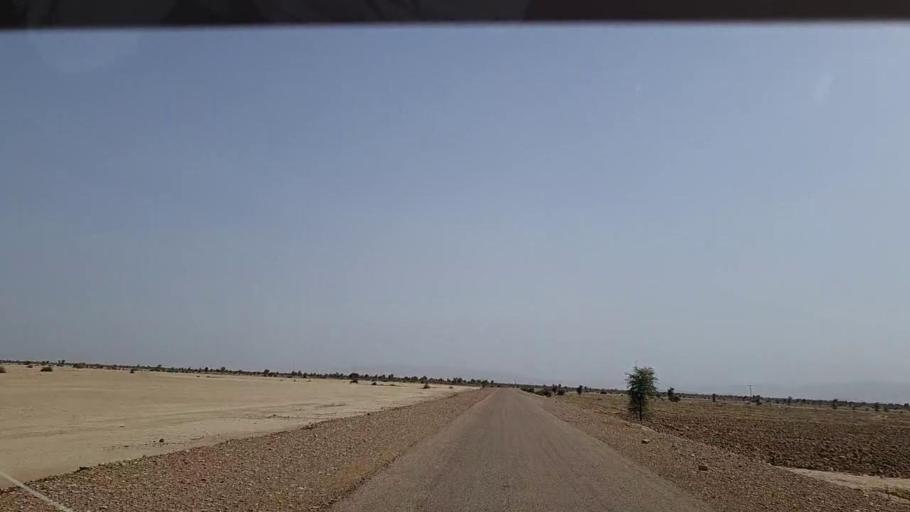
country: PK
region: Sindh
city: Johi
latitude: 26.6661
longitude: 67.5084
